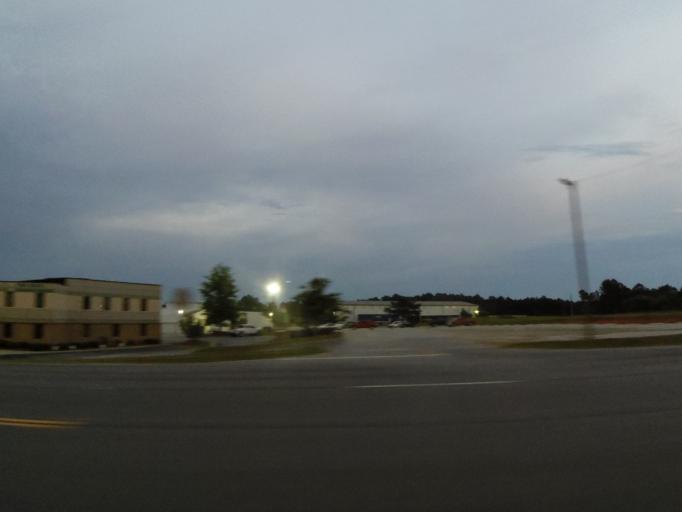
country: US
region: Georgia
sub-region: McDuffie County
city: Thomson
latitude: 33.5184
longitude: -82.5035
